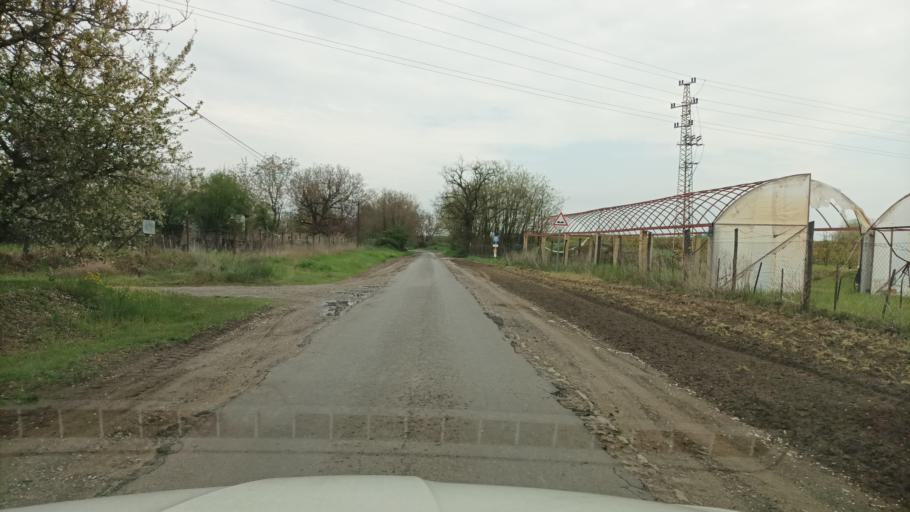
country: HU
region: Pest
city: Nagykoros
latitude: 47.0078
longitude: 19.7965
